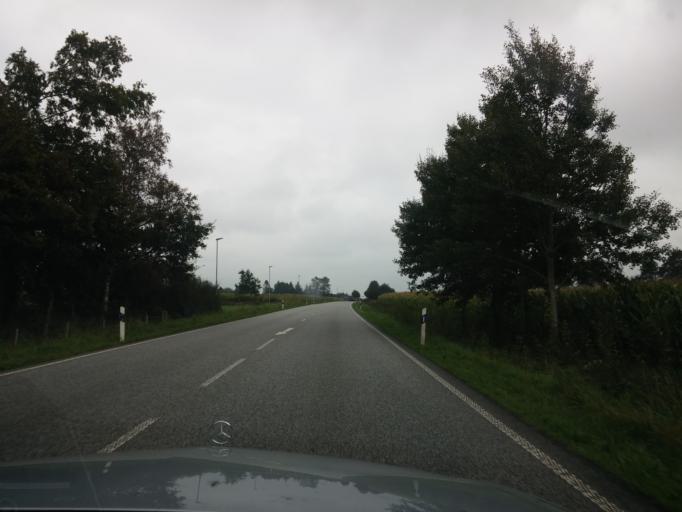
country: DE
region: Schleswig-Holstein
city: Oster-Ohrstedt
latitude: 54.5136
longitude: 9.2116
